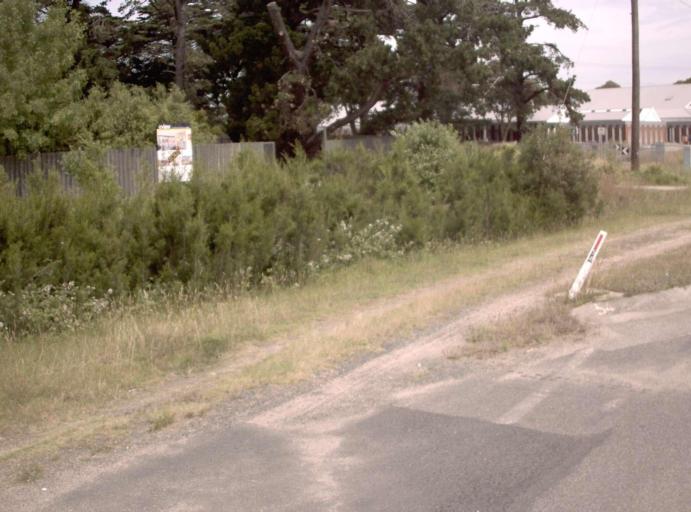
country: AU
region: Victoria
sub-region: Mornington Peninsula
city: Moorooduc
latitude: -38.2131
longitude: 145.1097
